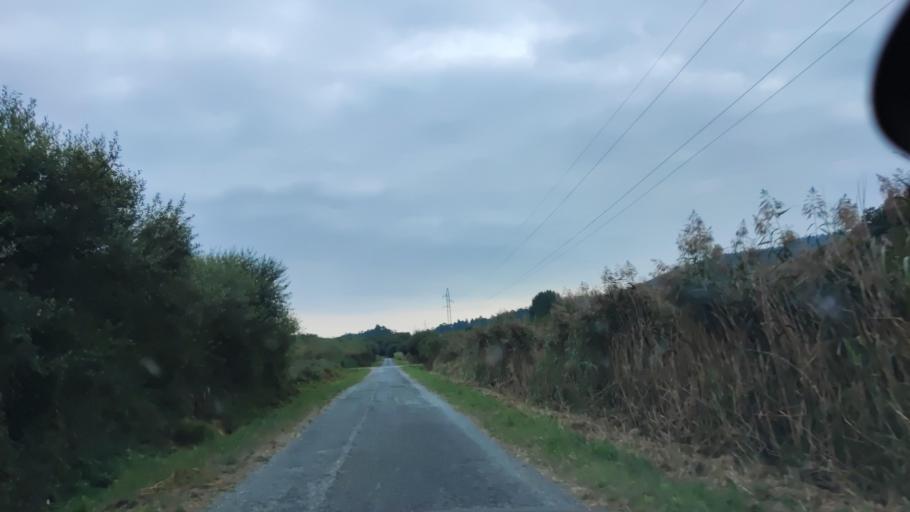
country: ES
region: Galicia
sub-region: Provincia de Pontevedra
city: Catoira
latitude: 42.7141
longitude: -8.7164
